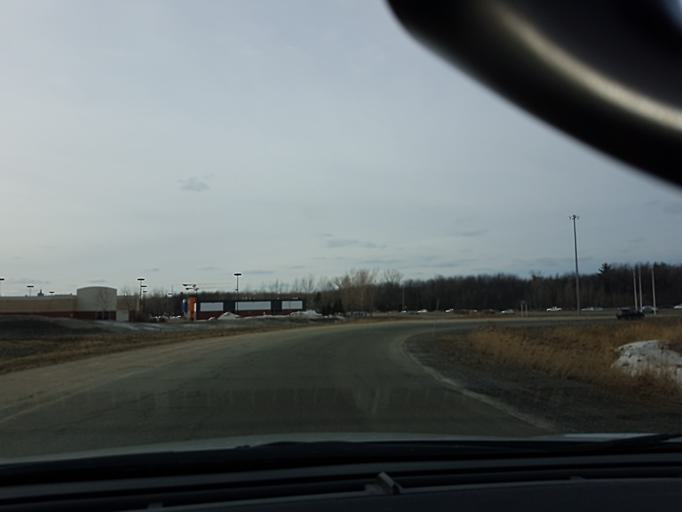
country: CA
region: Quebec
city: L'Ancienne-Lorette
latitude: 46.7820
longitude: -71.3431
